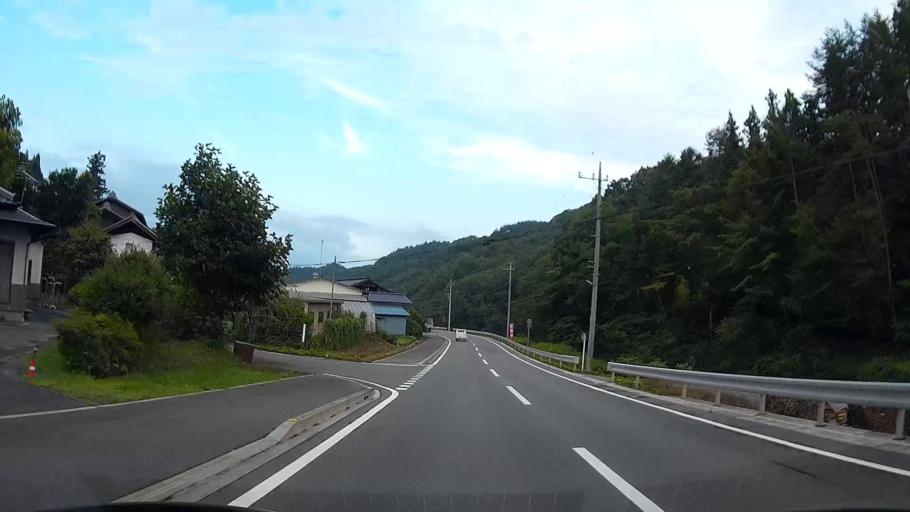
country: JP
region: Gunma
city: Nakanojomachi
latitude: 36.5280
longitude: 138.7214
